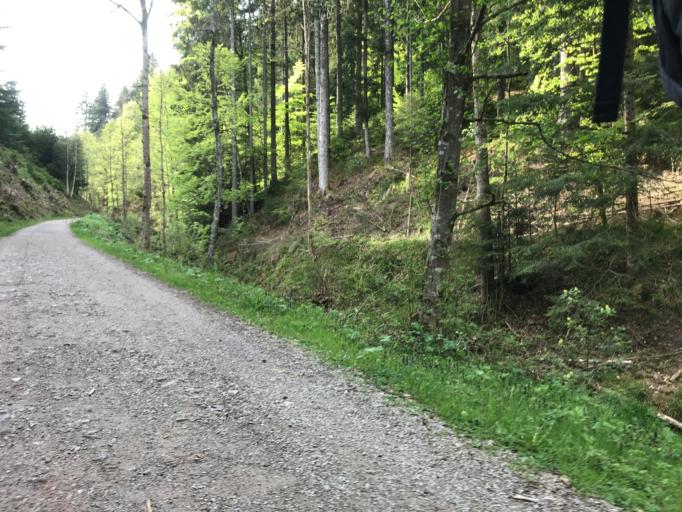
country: DE
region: Baden-Wuerttemberg
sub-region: Karlsruhe Region
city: Baiersbronn
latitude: 48.4833
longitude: 8.3442
